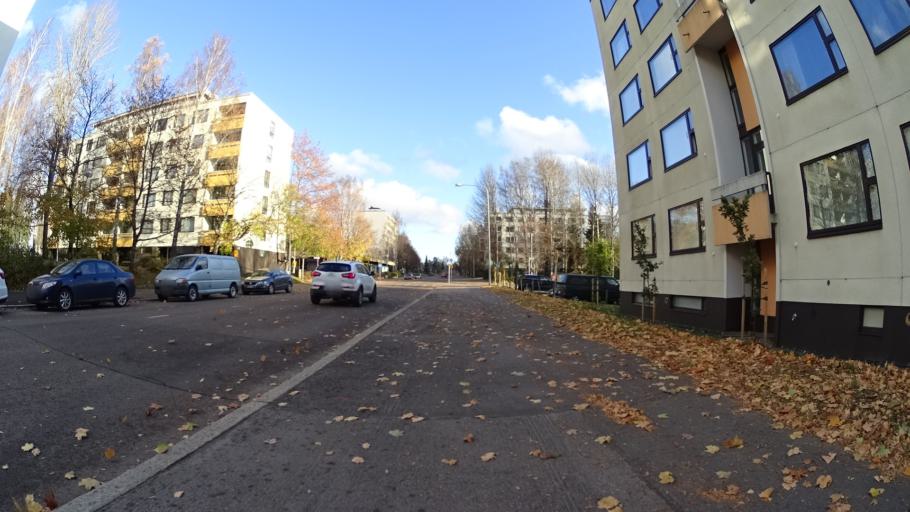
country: FI
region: Uusimaa
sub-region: Helsinki
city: Kilo
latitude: 60.2577
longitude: 24.8282
